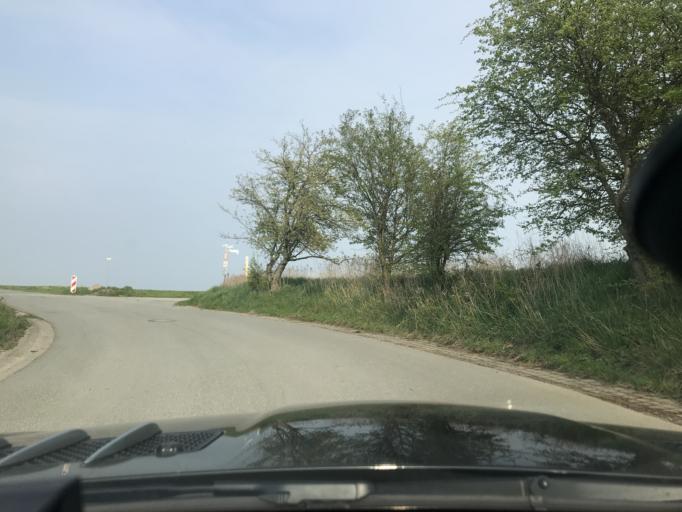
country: DE
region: Schleswig-Holstein
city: Fehmarn
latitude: 54.4908
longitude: 11.2206
